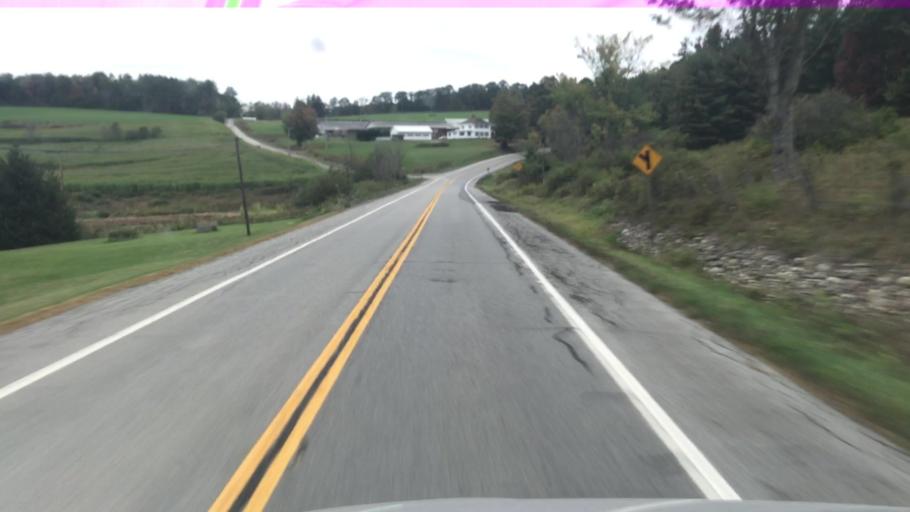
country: US
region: New York
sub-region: Otsego County
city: West End
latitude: 42.5323
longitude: -75.1805
